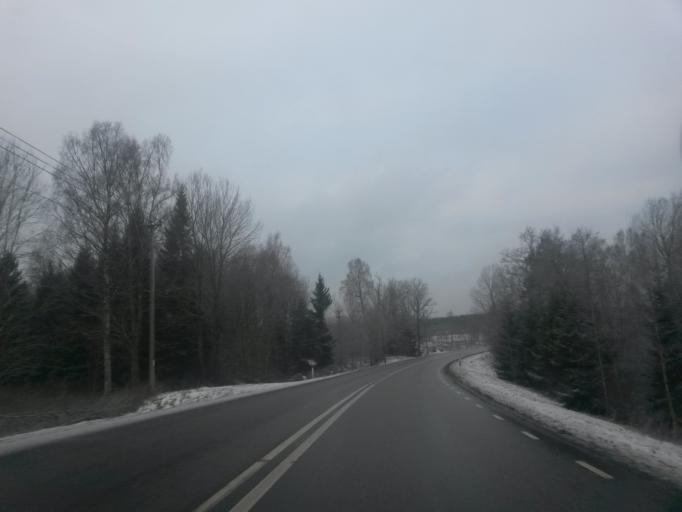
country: SE
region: Vaestra Goetaland
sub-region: Vargarda Kommun
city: Jonstorp
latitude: 58.0856
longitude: 12.6627
